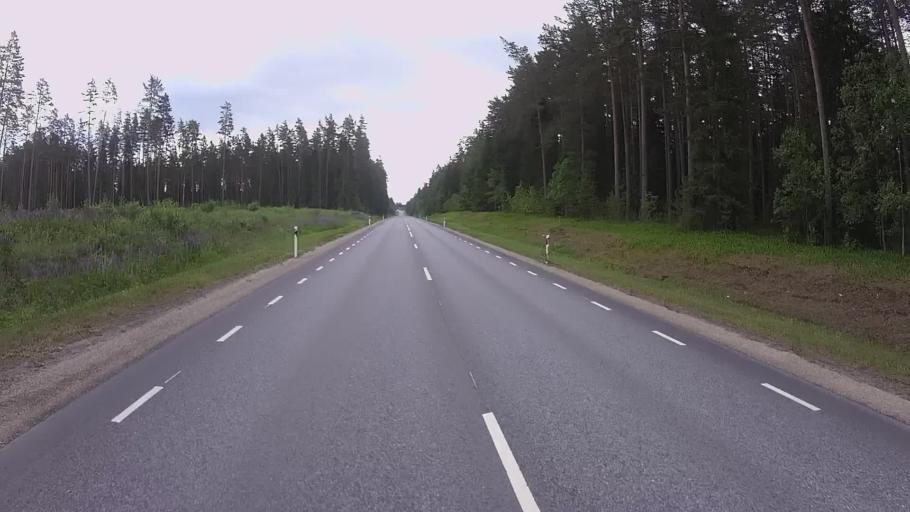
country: EE
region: Polvamaa
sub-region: Polva linn
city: Polva
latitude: 58.1037
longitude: 26.9925
